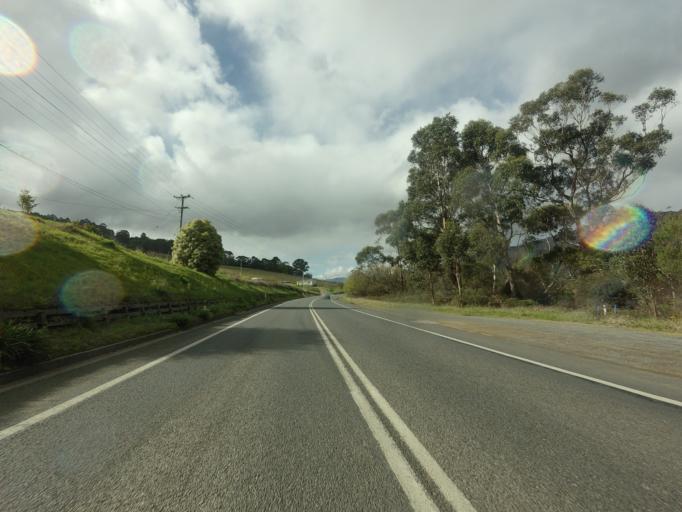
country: AU
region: Tasmania
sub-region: Huon Valley
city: Huonville
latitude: -43.0577
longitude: 147.0301
